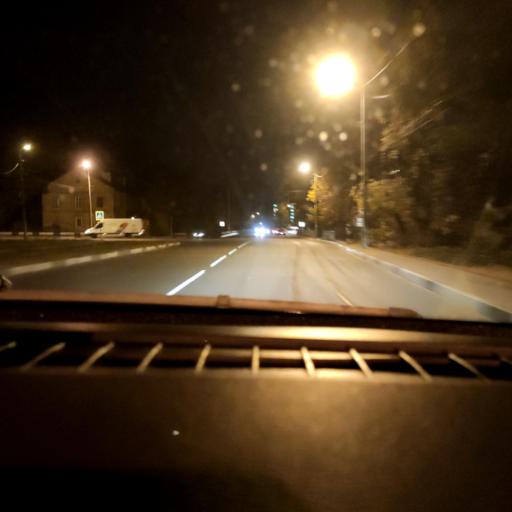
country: RU
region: Voronezj
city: Voronezh
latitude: 51.6936
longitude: 39.2085
